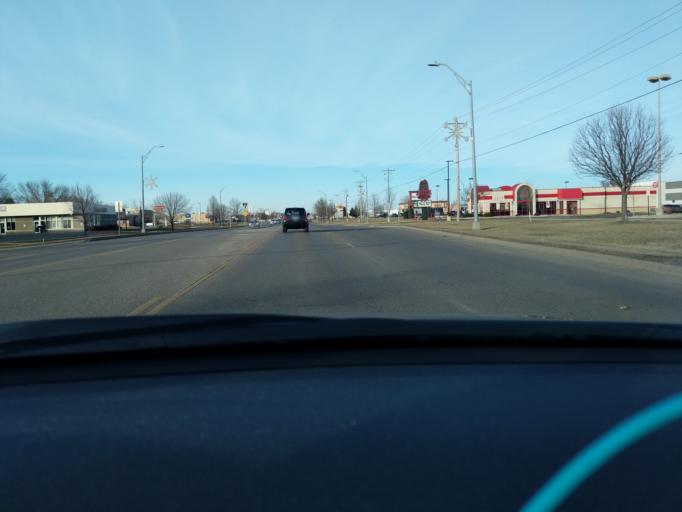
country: US
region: Minnesota
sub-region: Kandiyohi County
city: Willmar
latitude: 45.0981
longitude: -95.0426
